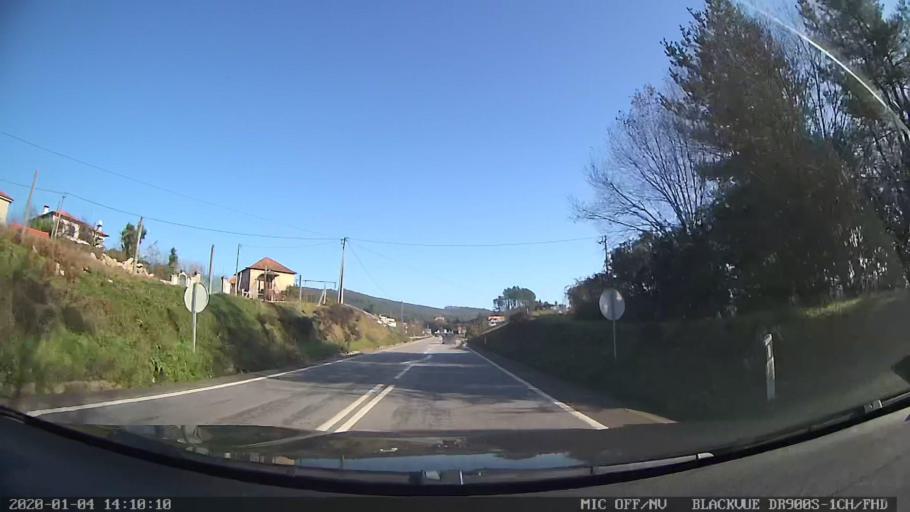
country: PT
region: Porto
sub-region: Amarante
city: Teloes
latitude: 41.3196
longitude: -8.0746
